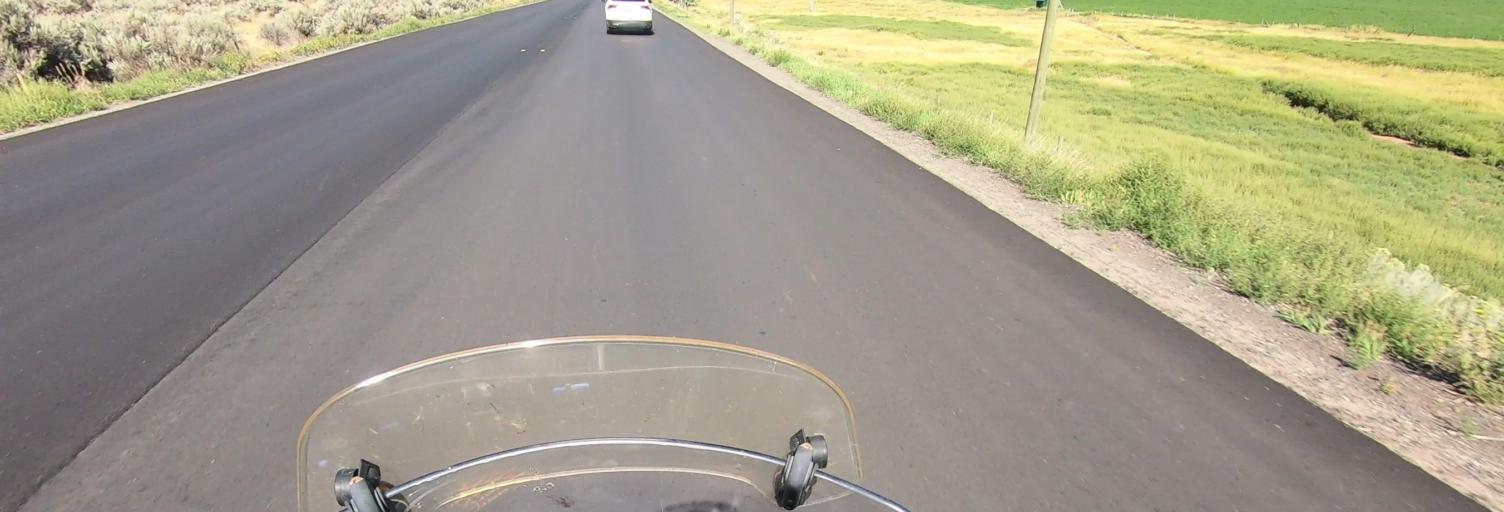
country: CA
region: British Columbia
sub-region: Thompson-Nicola Regional District
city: Ashcroft
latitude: 50.7916
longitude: -121.2391
